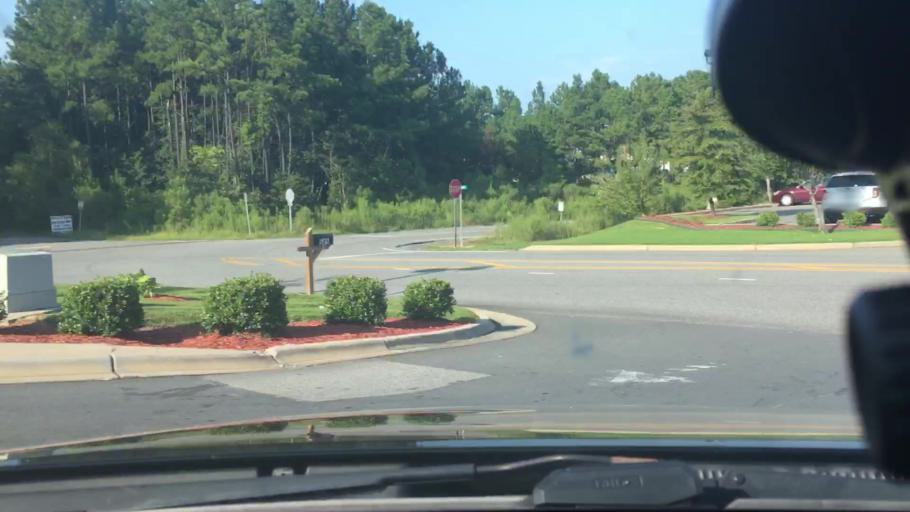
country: US
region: North Carolina
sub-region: Montgomery County
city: Biscoe
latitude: 35.3611
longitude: -79.7699
